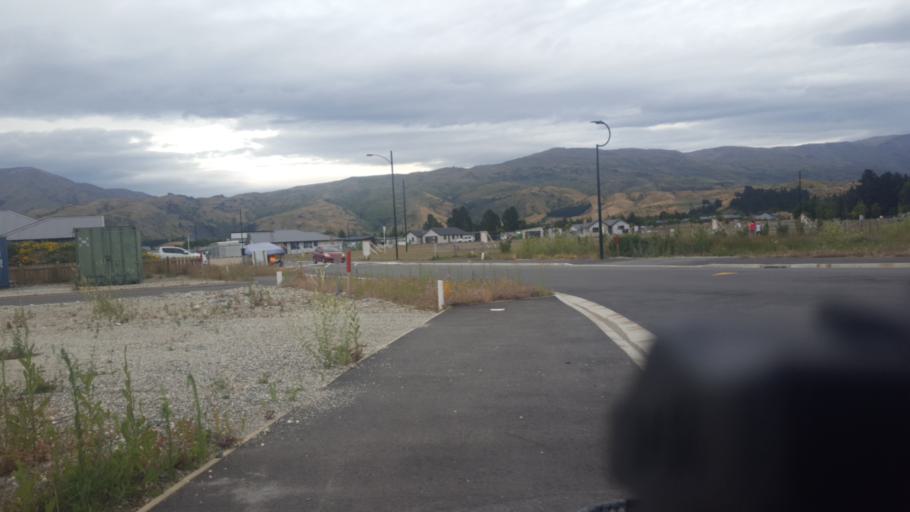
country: NZ
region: Otago
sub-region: Queenstown-Lakes District
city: Wanaka
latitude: -45.0488
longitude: 169.1928
